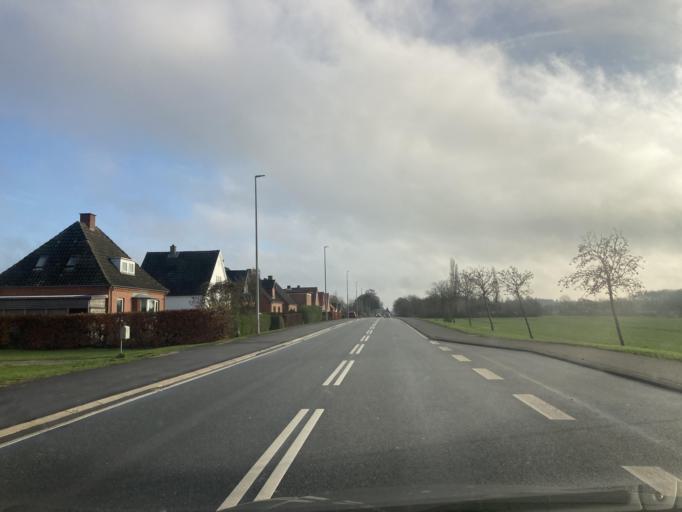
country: DK
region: Zealand
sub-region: Lolland Kommune
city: Maribo
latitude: 54.8056
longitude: 11.4341
